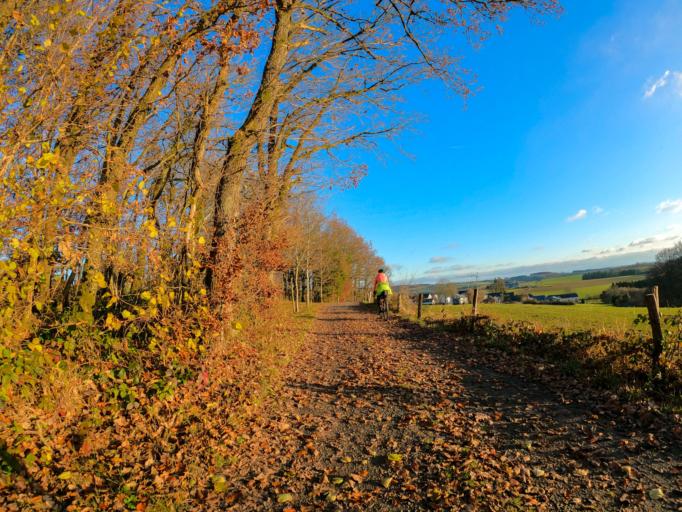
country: LU
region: Diekirch
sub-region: Canton de Wiltz
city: Bavigne
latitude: 49.9709
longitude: 5.8315
